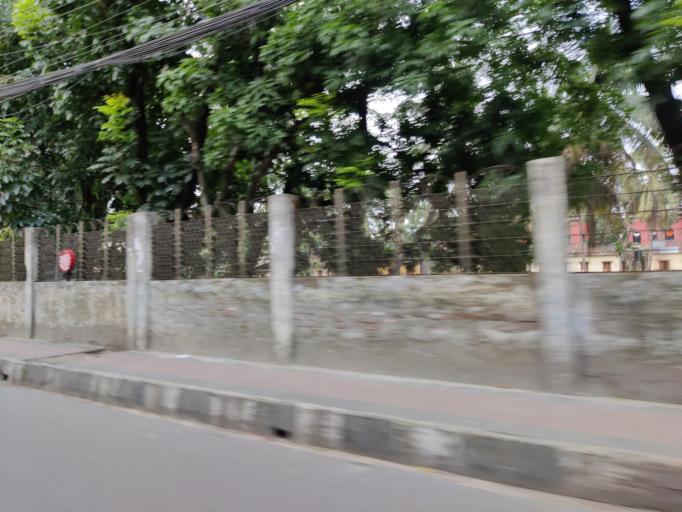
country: BD
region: Barisal
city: Barisal
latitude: 22.7073
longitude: 90.3710
